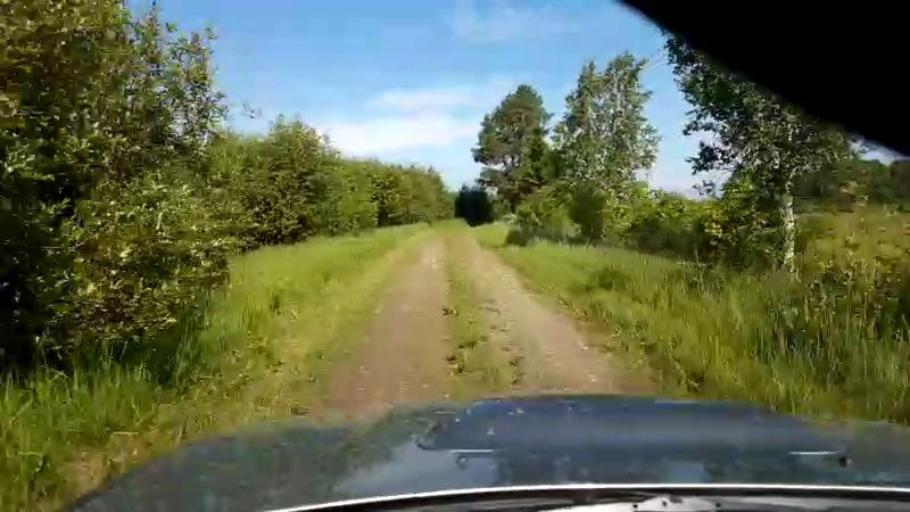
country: EE
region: Paernumaa
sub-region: Sindi linn
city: Sindi
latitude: 58.5002
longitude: 24.7008
